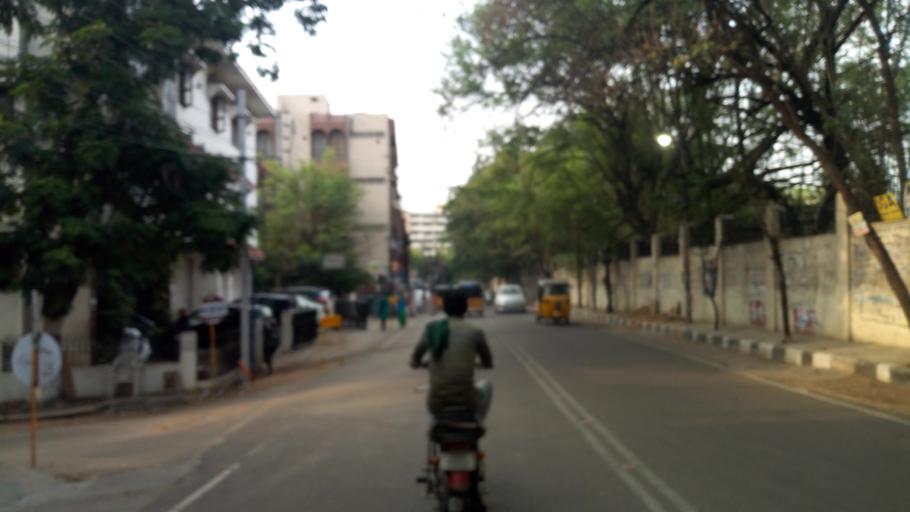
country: IN
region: Telangana
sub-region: Hyderabad
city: Hyderabad
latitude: 17.4049
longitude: 78.4726
